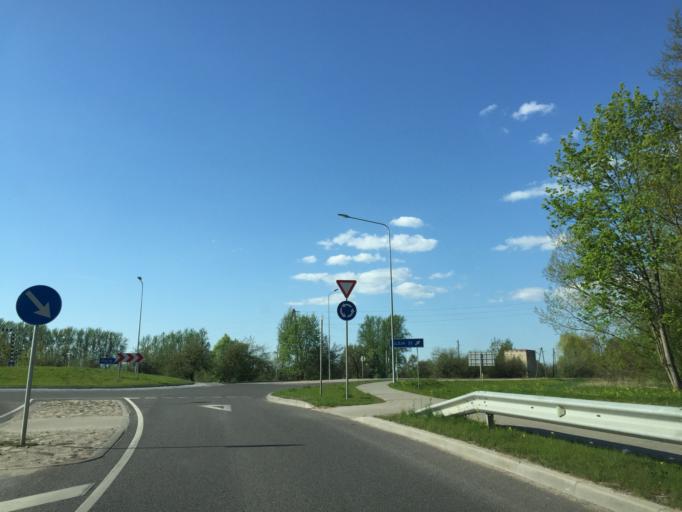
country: LV
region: Limbazu Rajons
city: Limbazi
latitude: 57.5157
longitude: 24.7252
